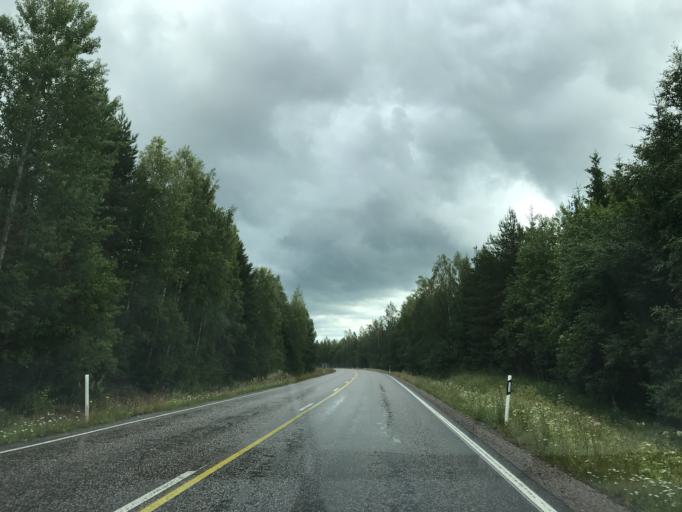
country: FI
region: Uusimaa
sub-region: Porvoo
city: Pukkila
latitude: 60.7704
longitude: 25.5369
